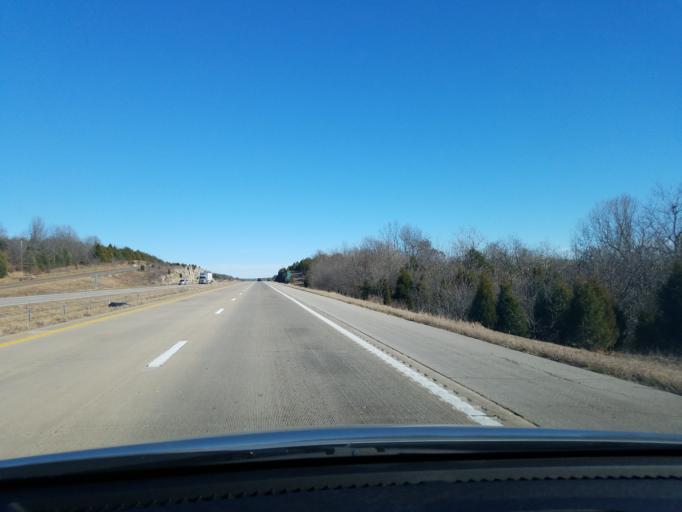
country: US
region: Missouri
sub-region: Laclede County
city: Lebanon
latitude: 37.7560
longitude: -92.5503
